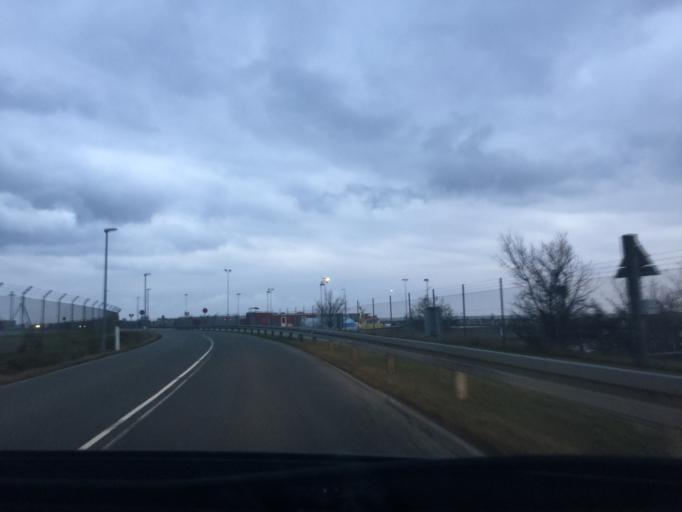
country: DK
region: Capital Region
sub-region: Dragor Kommune
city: Dragor
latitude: 55.6101
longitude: 12.6797
